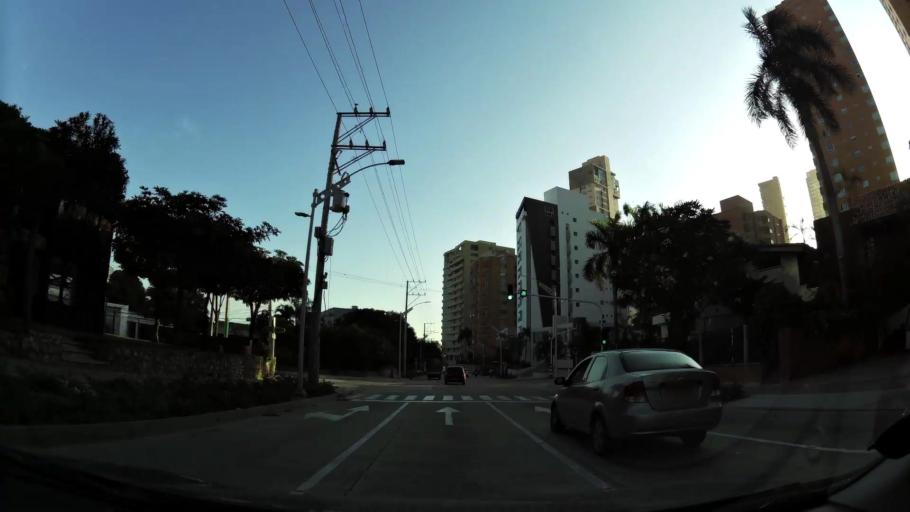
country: CO
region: Atlantico
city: Barranquilla
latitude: 11.0093
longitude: -74.8135
